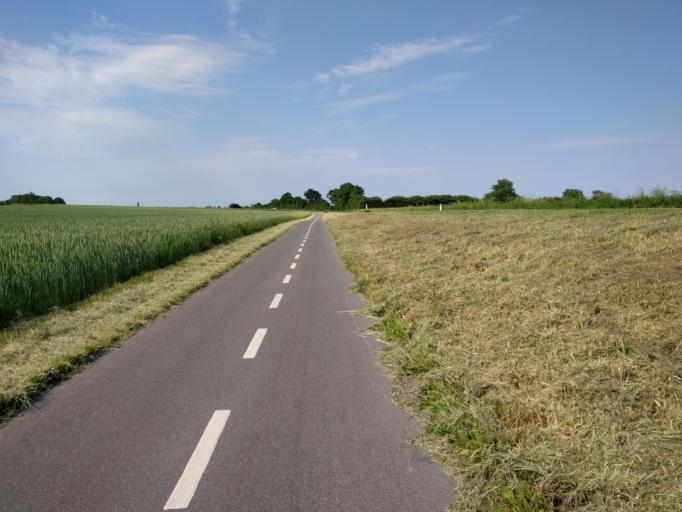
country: DK
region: South Denmark
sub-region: Kerteminde Kommune
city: Kerteminde
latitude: 55.4289
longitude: 10.6527
